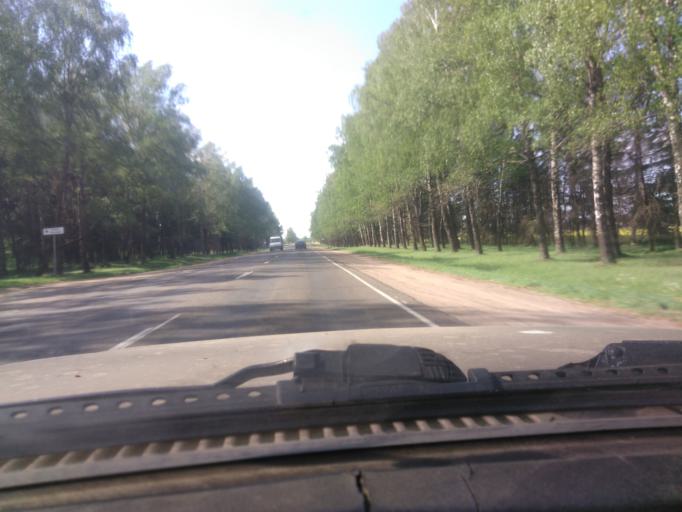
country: BY
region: Mogilev
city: Buynichy
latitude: 53.8445
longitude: 30.2502
